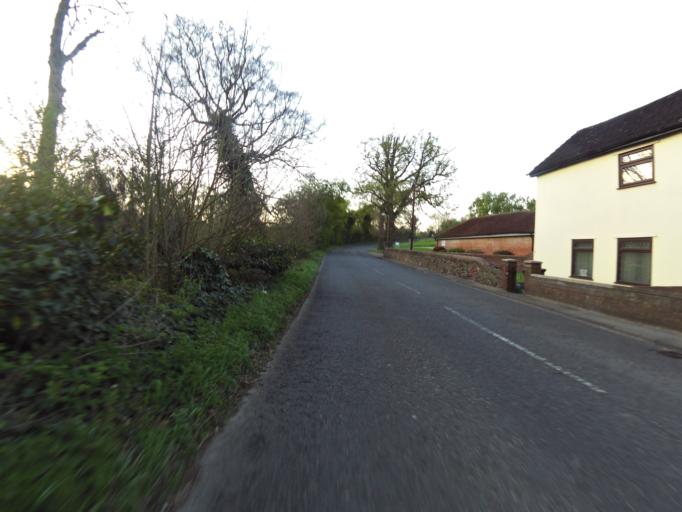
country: GB
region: England
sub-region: Suffolk
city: Bramford
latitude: 52.0561
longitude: 1.0962
